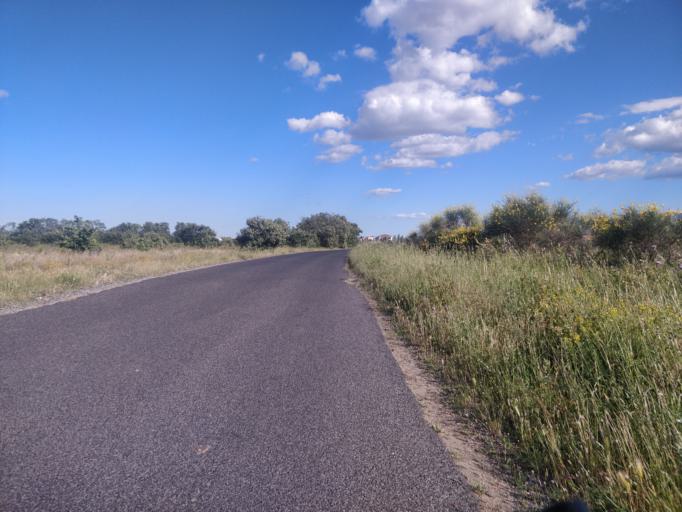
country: FR
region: Languedoc-Roussillon
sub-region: Departement des Pyrenees-Orientales
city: Cabestany
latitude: 42.6651
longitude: 2.9356
